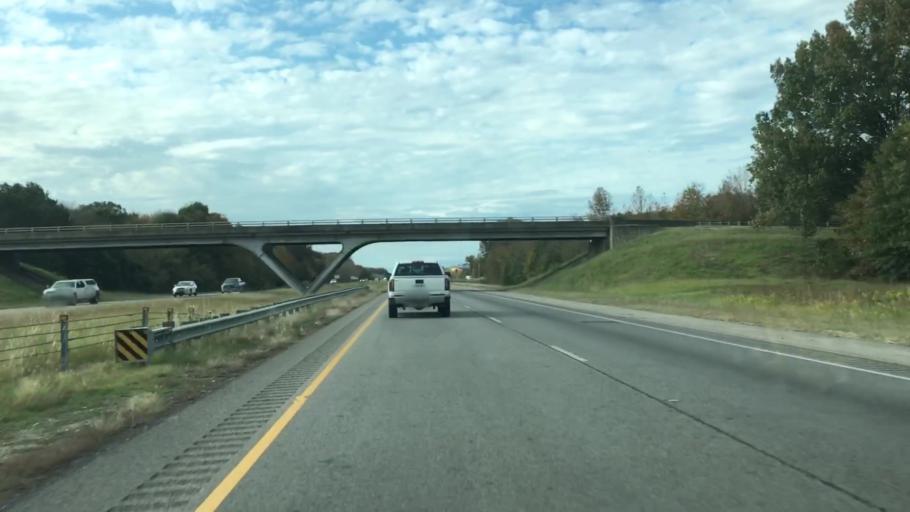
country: US
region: Arkansas
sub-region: Conway County
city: Morrilton
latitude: 35.2189
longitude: -92.8293
